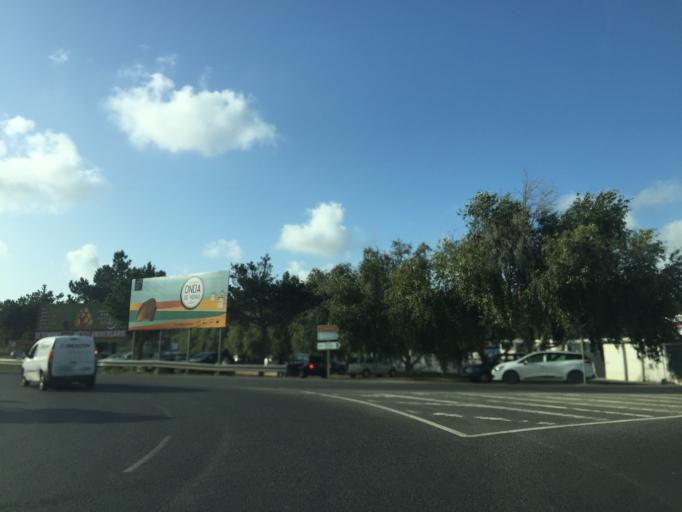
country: PT
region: Lisbon
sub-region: Torres Vedras
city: Torres Vedras
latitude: 39.0918
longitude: -9.2662
